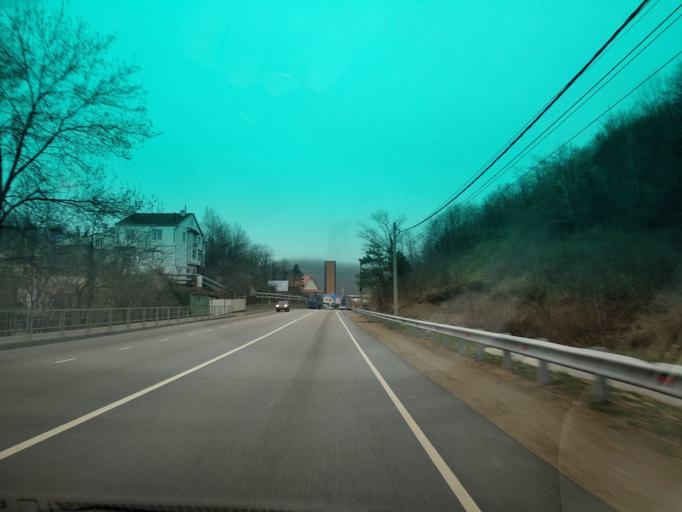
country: RU
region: Krasnodarskiy
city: Tuapse
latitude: 44.1110
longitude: 39.0723
